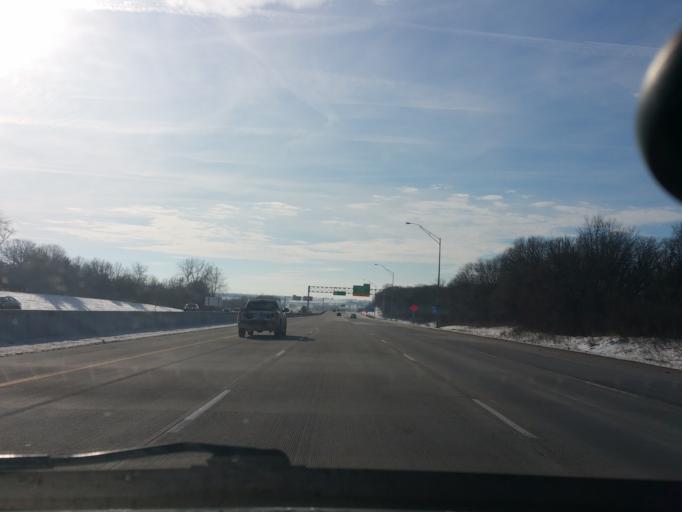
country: US
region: Iowa
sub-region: Polk County
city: West Des Moines
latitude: 41.5544
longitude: -93.7765
